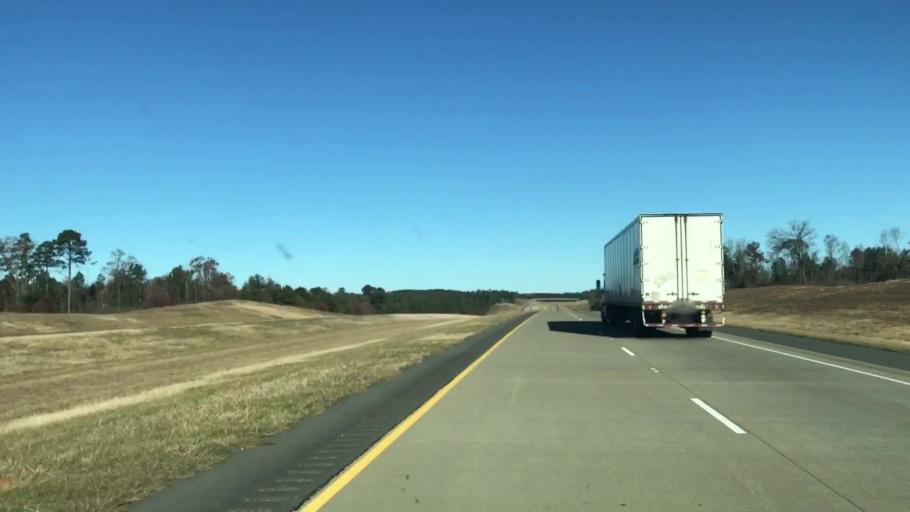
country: US
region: Louisiana
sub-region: Caddo Parish
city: Vivian
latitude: 32.9587
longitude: -93.9022
